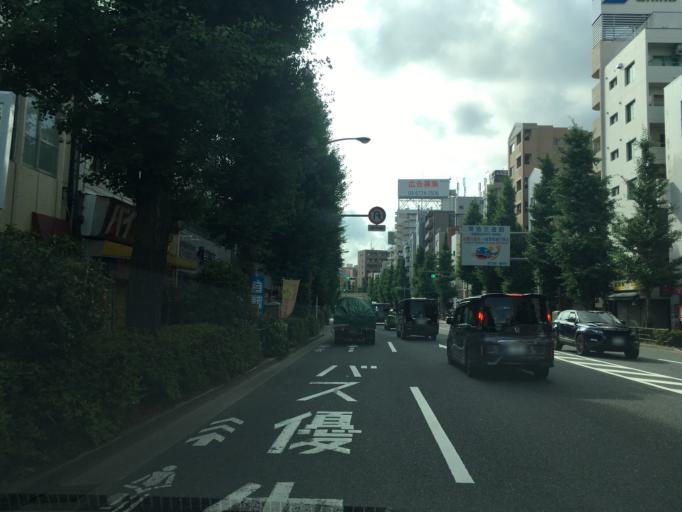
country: JP
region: Tokyo
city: Tokyo
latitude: 35.6987
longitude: 139.6376
